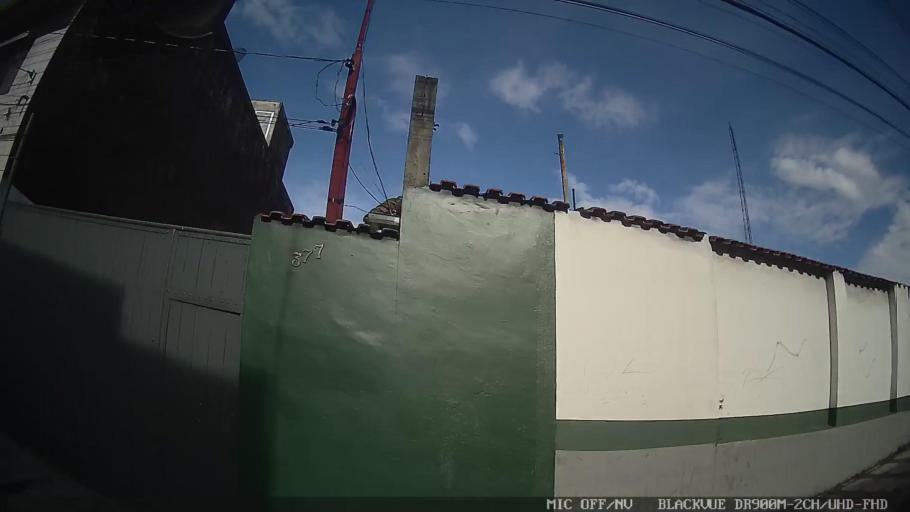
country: BR
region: Sao Paulo
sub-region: Mogi das Cruzes
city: Mogi das Cruzes
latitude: -23.5256
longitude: -46.1886
